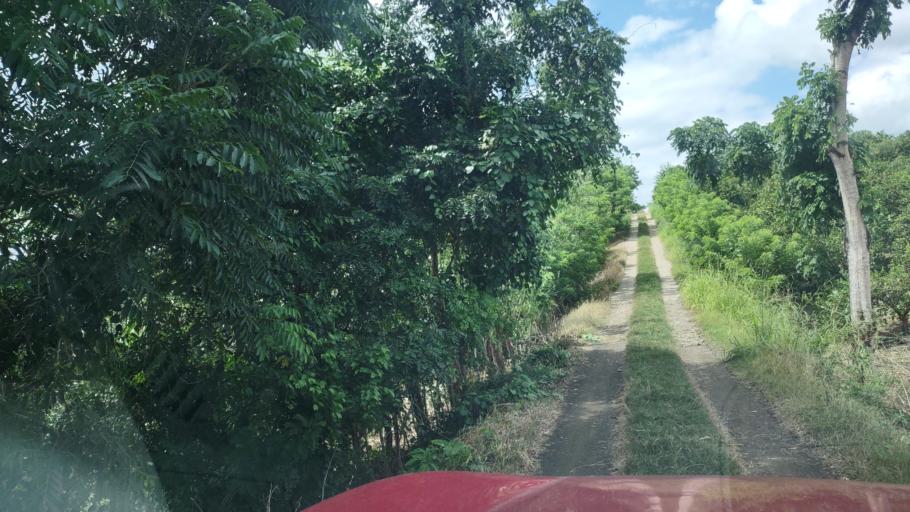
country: MX
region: Puebla
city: San Jose Acateno
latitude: 20.2226
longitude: -97.1516
